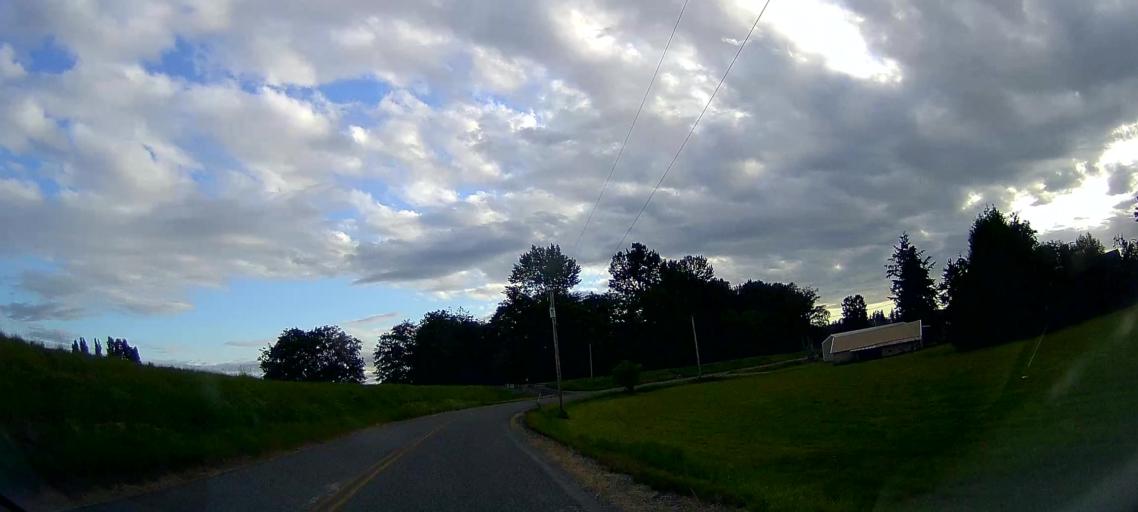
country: US
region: Washington
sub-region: Skagit County
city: Mount Vernon
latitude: 48.3678
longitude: -122.4084
